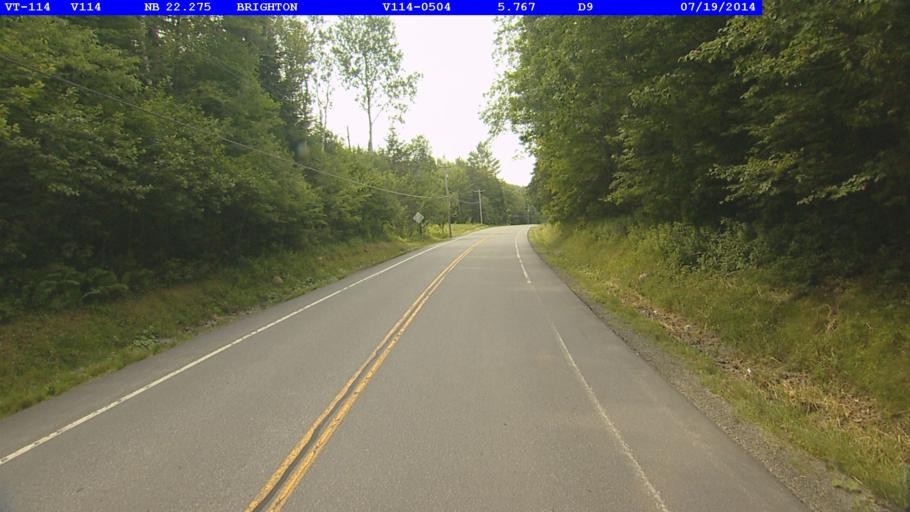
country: US
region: Vermont
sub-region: Caledonia County
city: Lyndonville
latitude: 44.8259
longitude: -71.9019
